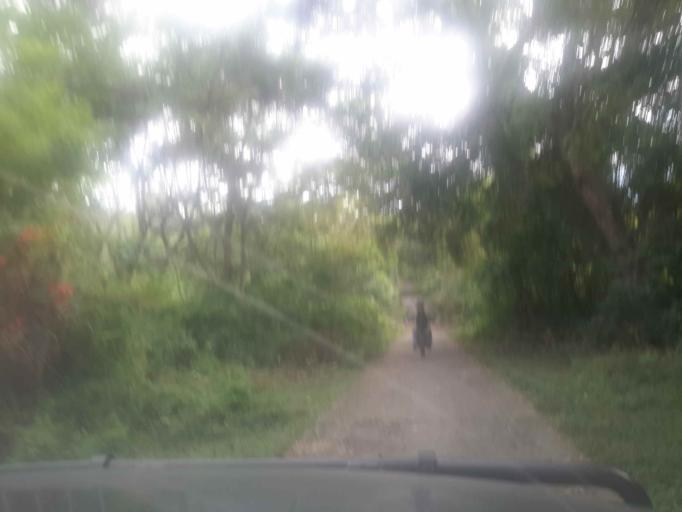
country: NI
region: Rivas
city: Altagracia
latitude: 11.5111
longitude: -85.6071
